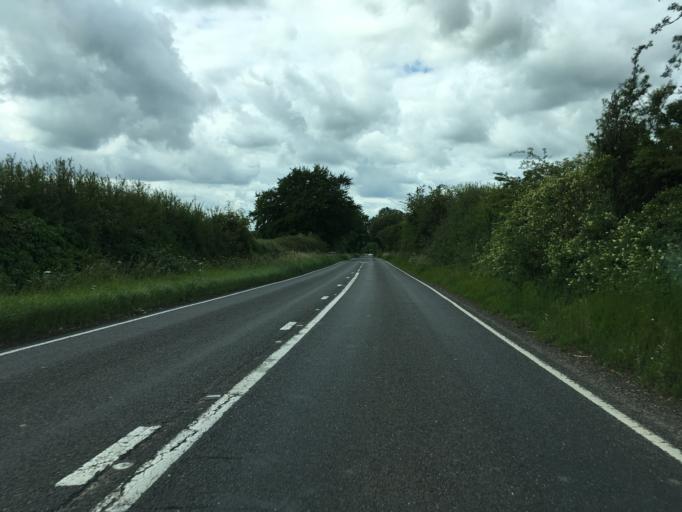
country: GB
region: England
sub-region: Oxfordshire
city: Shipton under Wychwood
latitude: 51.8879
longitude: -1.5682
